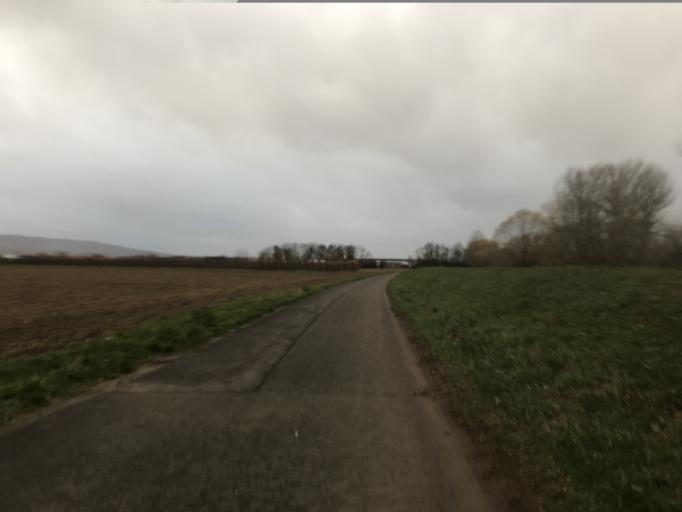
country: DE
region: Rheinland-Pfalz
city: Oestrich-Winkel
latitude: 49.9815
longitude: 8.0065
